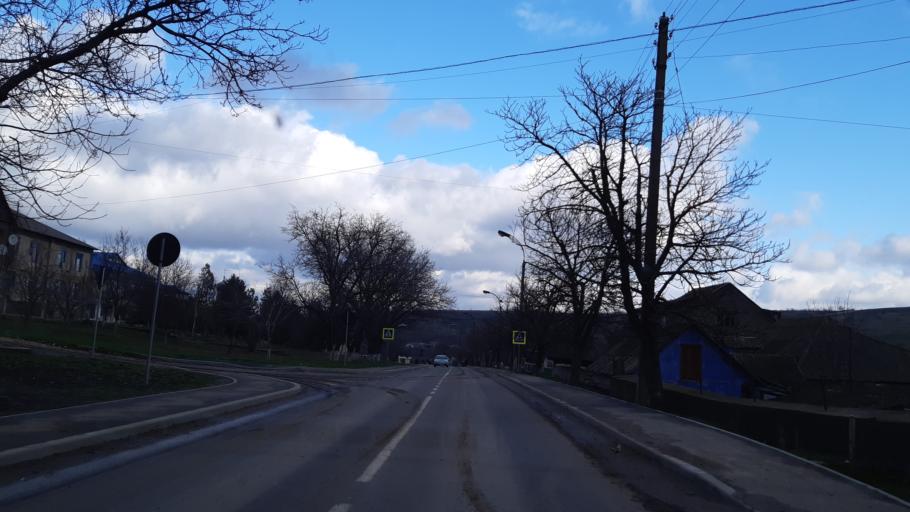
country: MD
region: Telenesti
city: Cocieri
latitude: 47.2201
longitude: 29.0241
